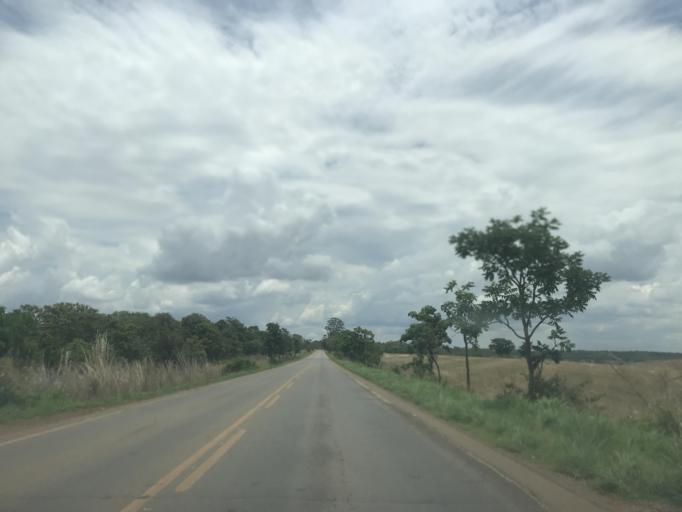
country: BR
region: Goias
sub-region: Vianopolis
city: Vianopolis
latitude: -16.7280
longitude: -48.4402
